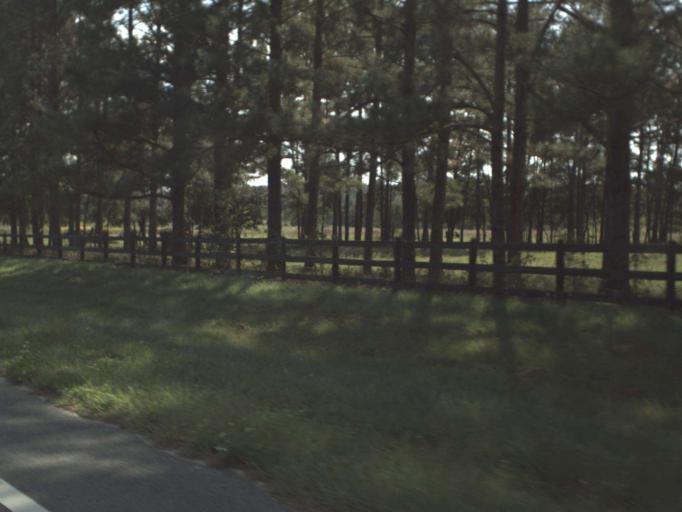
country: US
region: Florida
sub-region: Jefferson County
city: Monticello
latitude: 30.4526
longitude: -84.0187
